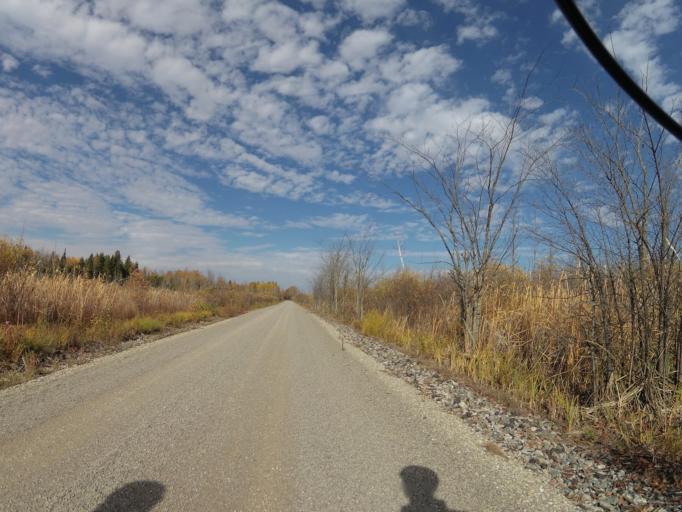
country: CA
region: Ontario
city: Carleton Place
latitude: 45.0274
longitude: -76.0783
